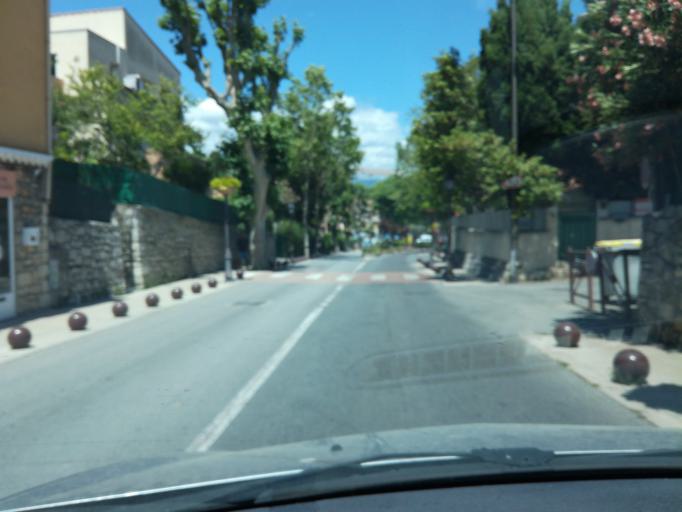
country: FR
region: Provence-Alpes-Cote d'Azur
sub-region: Departement des Alpes-Maritimes
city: Mougins
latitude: 43.5995
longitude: 6.9861
